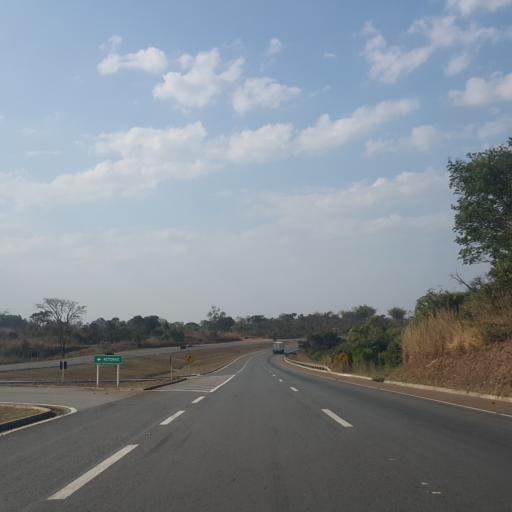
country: BR
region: Goias
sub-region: Abadiania
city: Abadiania
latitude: -16.1774
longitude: -48.6505
